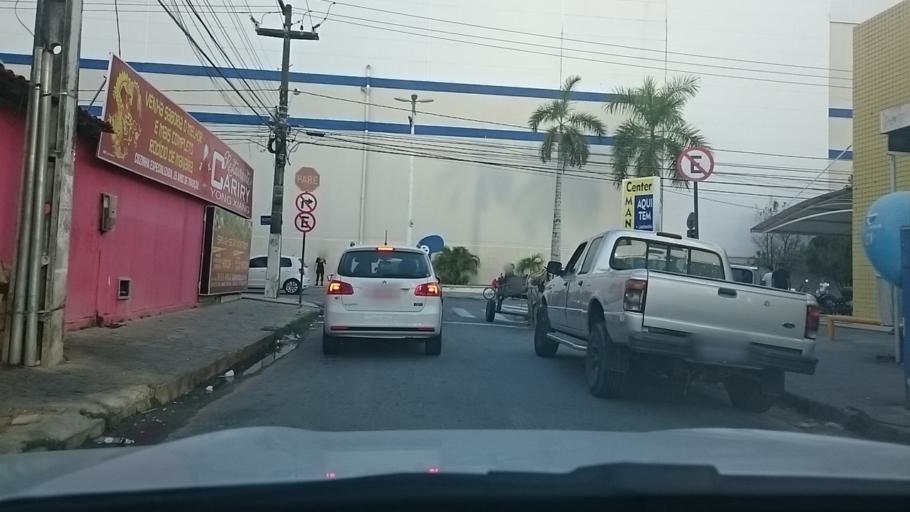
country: BR
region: Paraiba
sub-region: Joao Pessoa
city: Joao Pessoa
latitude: -7.0994
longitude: -34.8436
